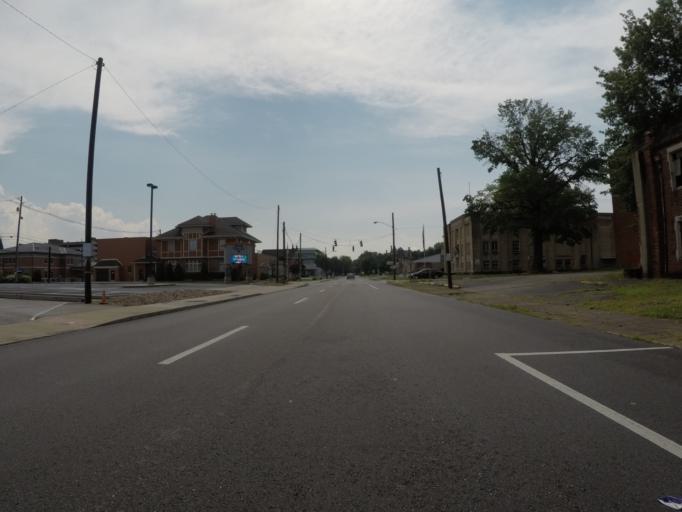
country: US
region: Kentucky
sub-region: Boyd County
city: Ashland
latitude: 38.4777
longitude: -82.6427
